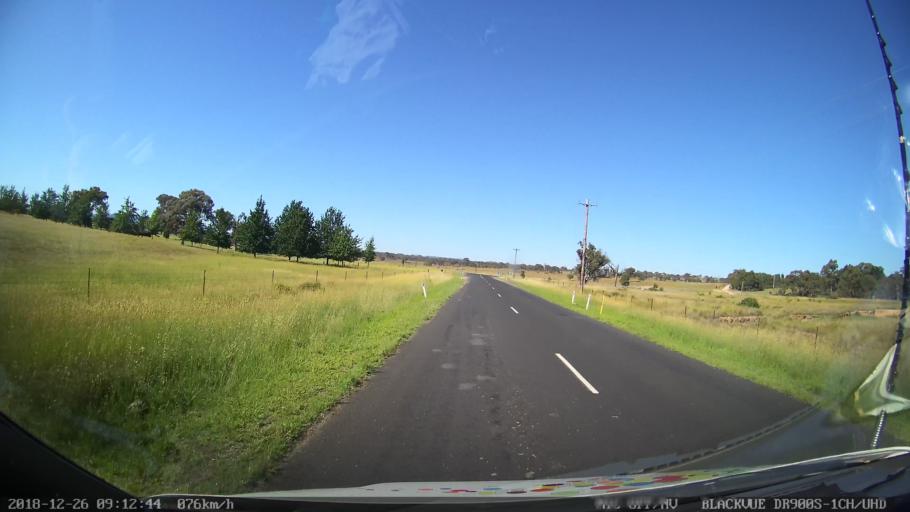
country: AU
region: New South Wales
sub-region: Mid-Western Regional
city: Kandos
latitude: -32.7607
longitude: 149.9800
